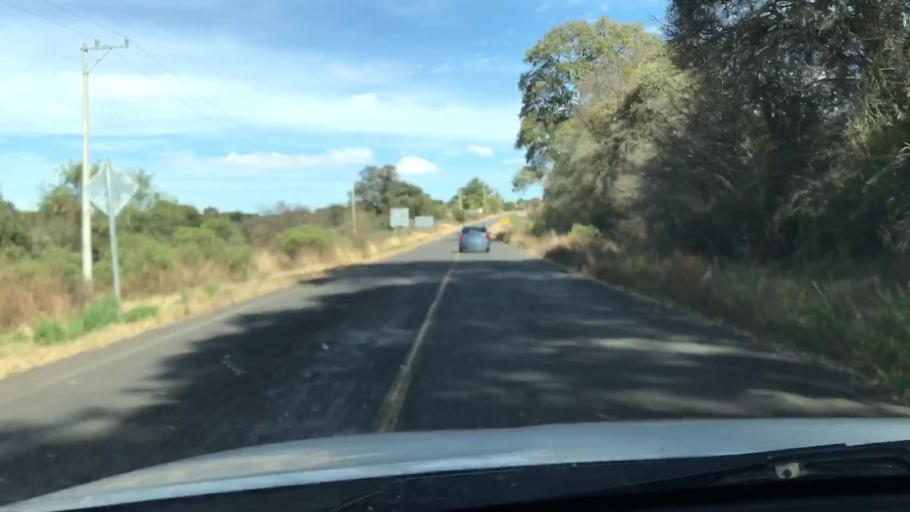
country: MX
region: Jalisco
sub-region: Zacoalco de Torres
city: Barranca de Otates (Barranca de Otatan)
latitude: 20.1933
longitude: -103.7199
